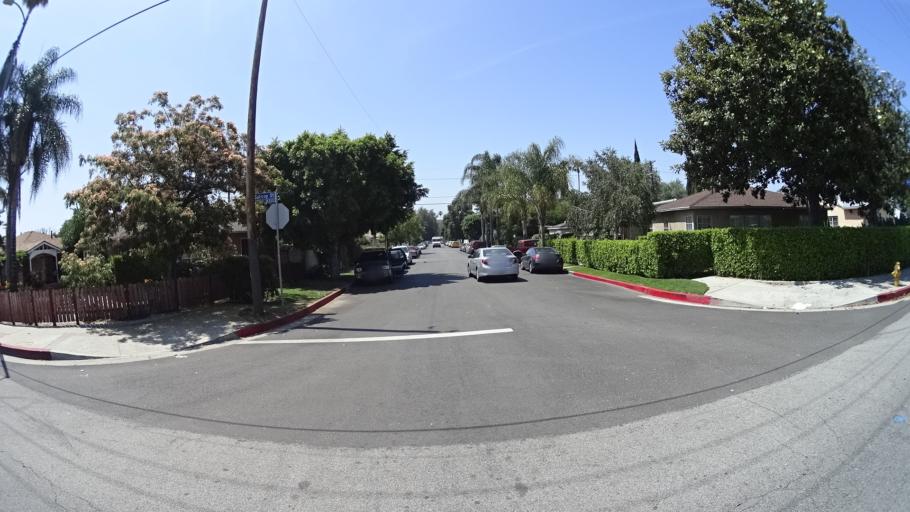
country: US
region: California
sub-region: Los Angeles County
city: Van Nuys
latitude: 34.2084
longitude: -118.4553
